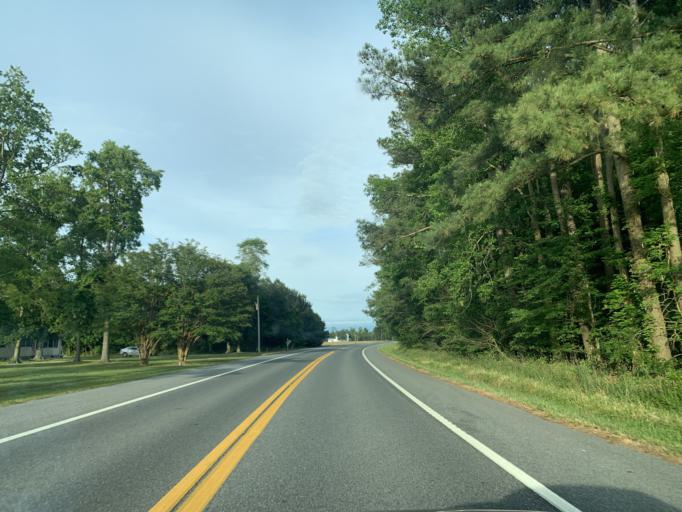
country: US
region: Virginia
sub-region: Accomack County
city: Captains Cove
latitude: 38.0698
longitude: -75.4520
